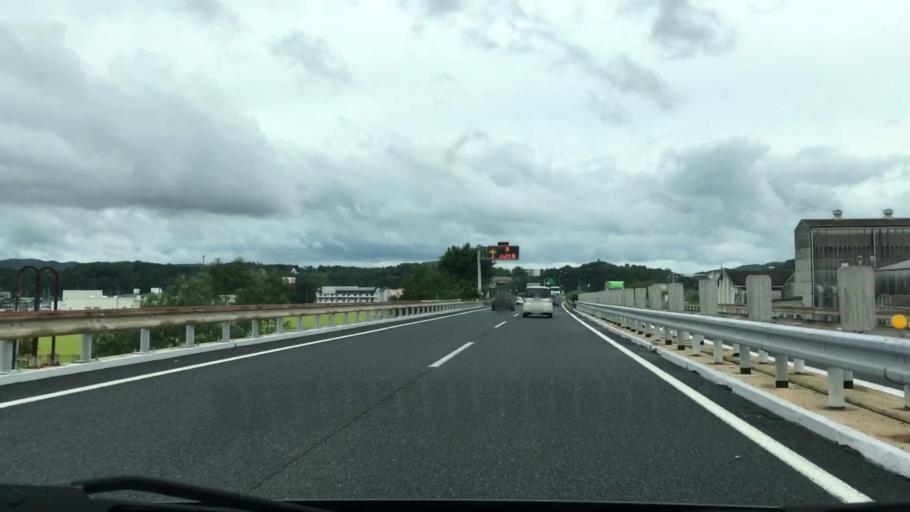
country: JP
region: Okayama
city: Tsuyama
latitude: 35.0240
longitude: 134.1691
